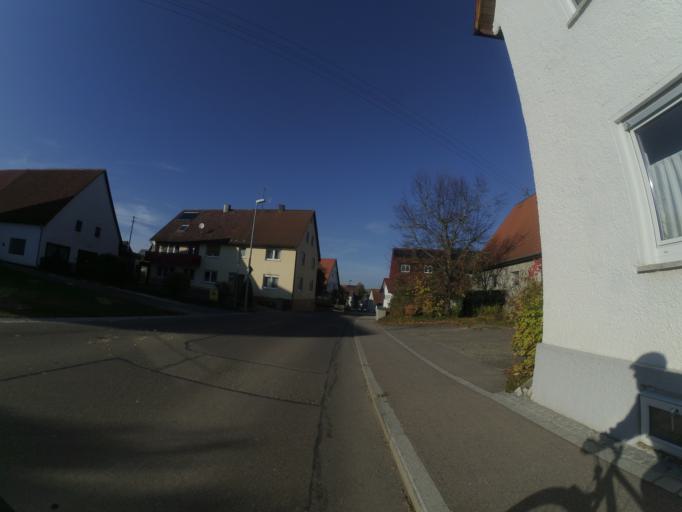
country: DE
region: Baden-Wuerttemberg
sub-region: Tuebingen Region
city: Blaubeuren
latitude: 48.4362
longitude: 9.8183
